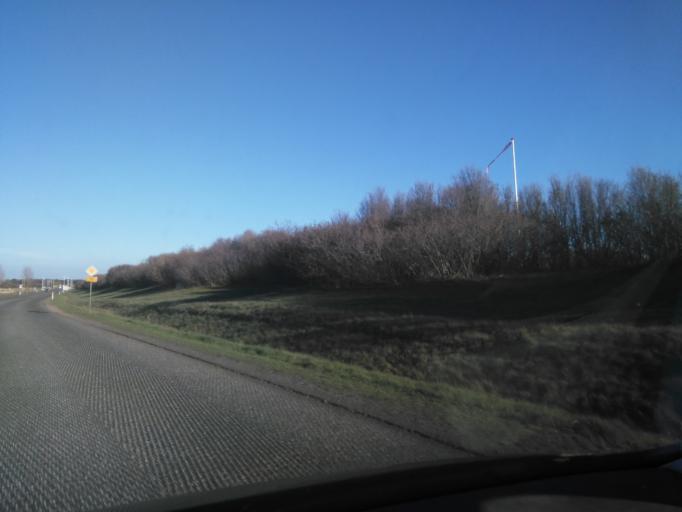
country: DK
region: Central Jutland
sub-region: Ringkobing-Skjern Kommune
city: Videbaek
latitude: 56.0984
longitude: 8.6331
